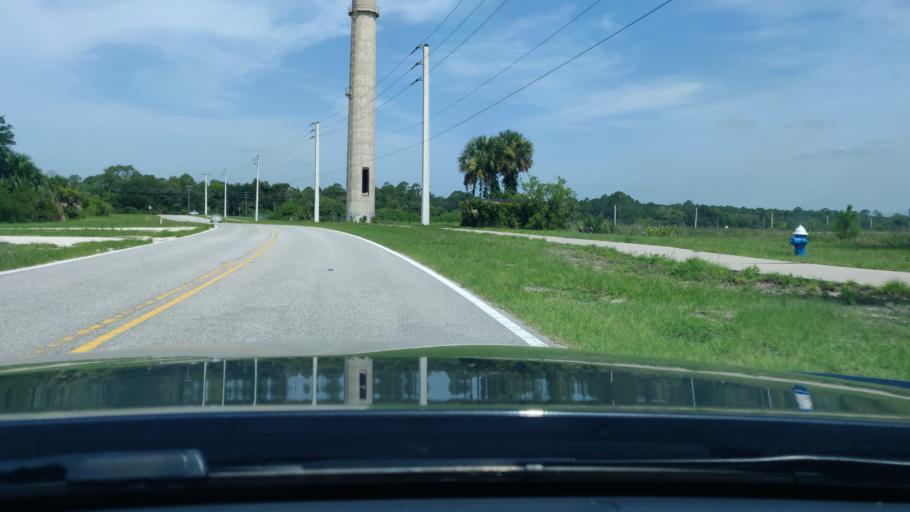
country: US
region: Florida
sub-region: Flagler County
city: Flagler Beach
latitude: 29.4938
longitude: -81.1545
